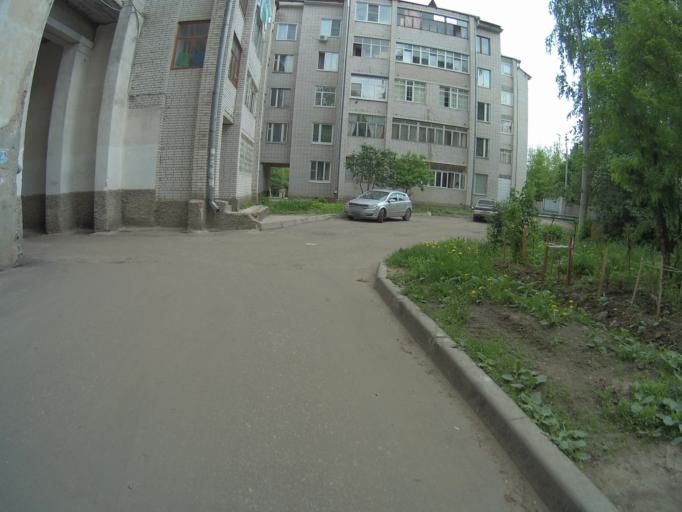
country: RU
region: Vladimir
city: Vladimir
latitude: 56.1312
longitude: 40.3936
